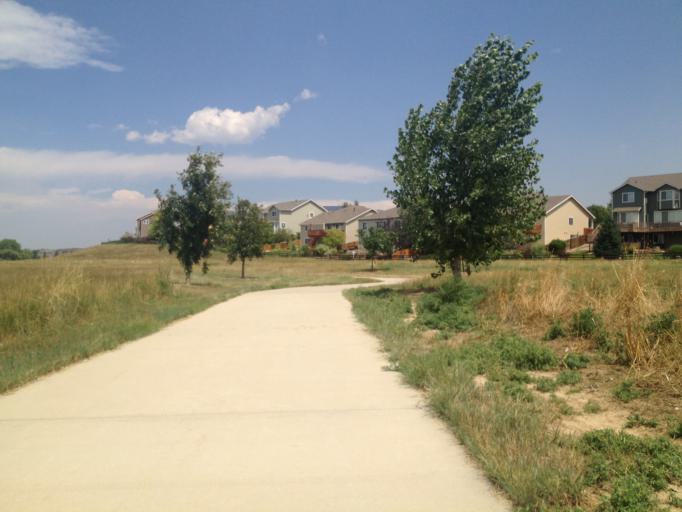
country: US
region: Colorado
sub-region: Boulder County
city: Erie
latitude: 40.0224
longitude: -105.0443
